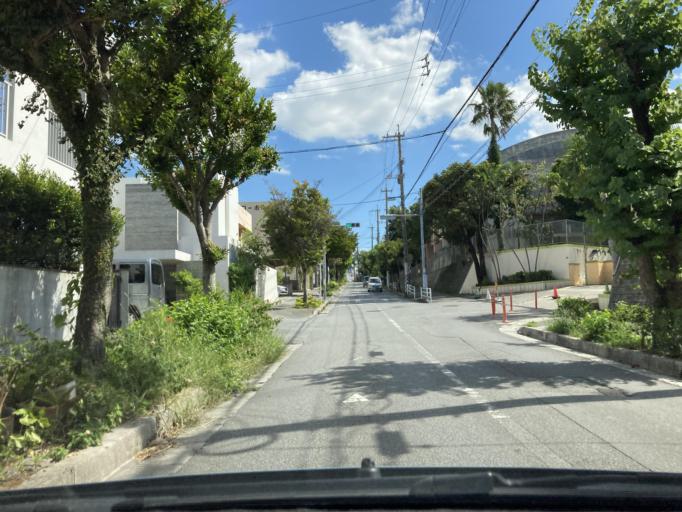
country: JP
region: Okinawa
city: Naha-shi
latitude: 26.2004
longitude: 127.6923
